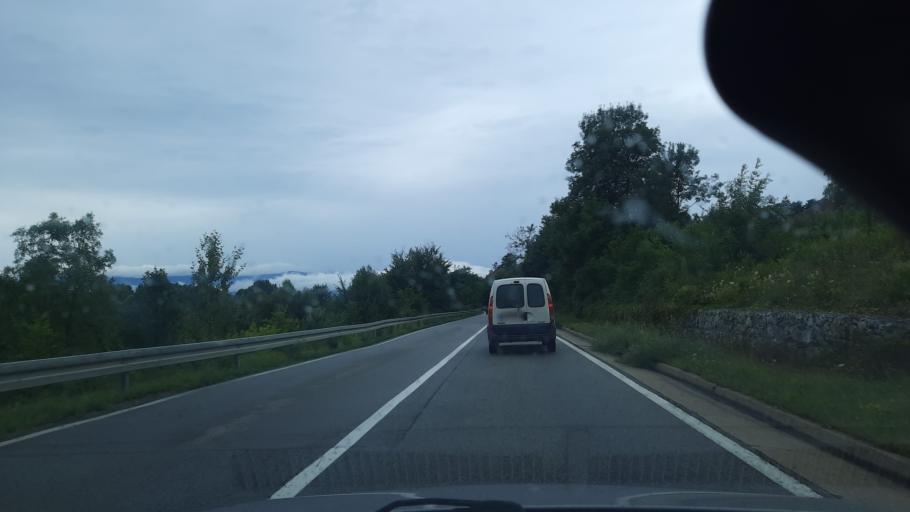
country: RS
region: Central Serbia
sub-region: Raski Okrug
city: Kraljevo
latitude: 43.7644
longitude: 20.8064
